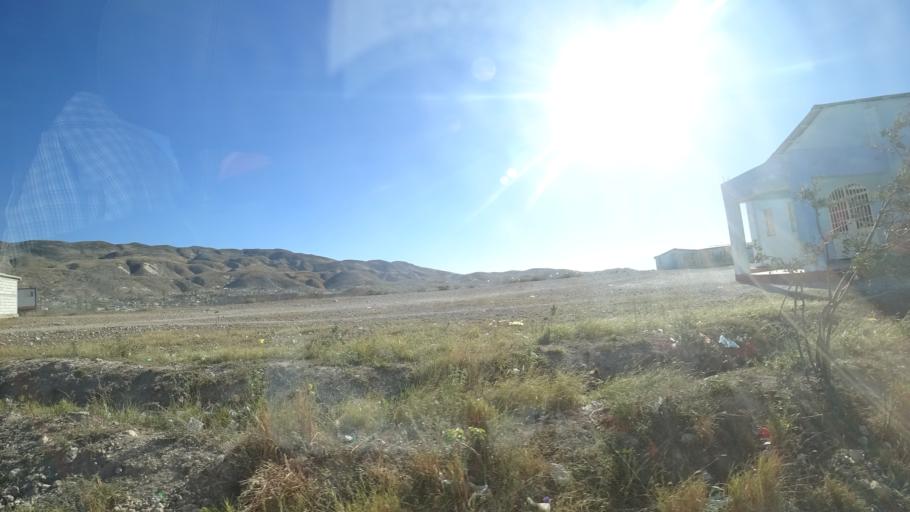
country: HT
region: Ouest
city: Cabaret
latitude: 18.6859
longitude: -72.3217
